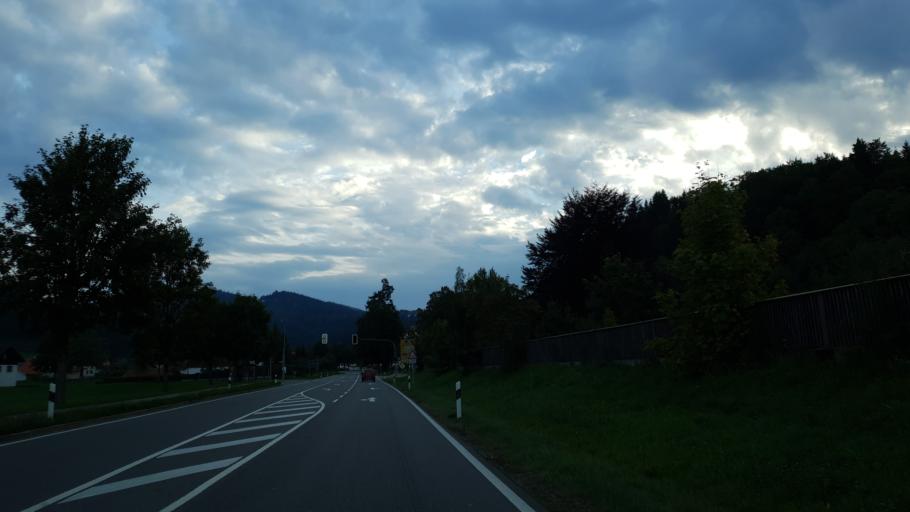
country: DE
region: Bavaria
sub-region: Swabia
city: Weitnau
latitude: 47.6617
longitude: 10.0938
